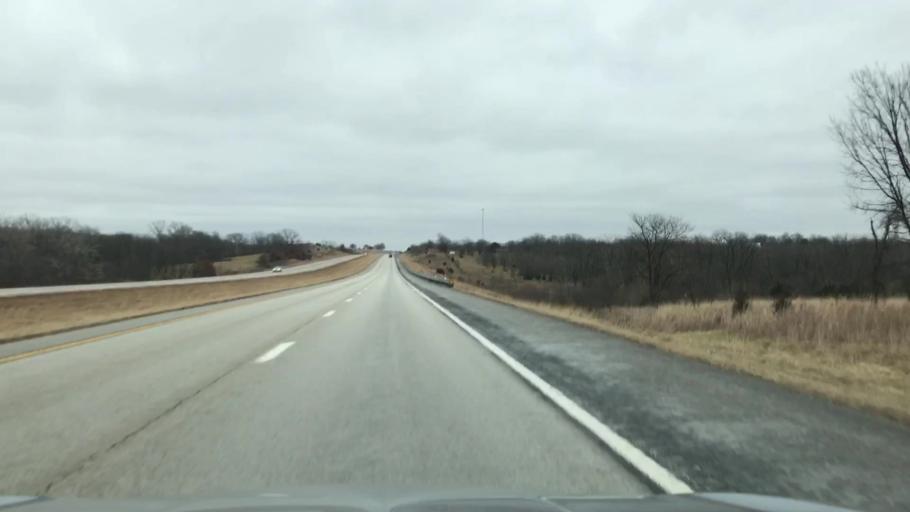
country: US
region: Missouri
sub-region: Caldwell County
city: Hamilton
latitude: 39.7493
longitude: -94.0735
